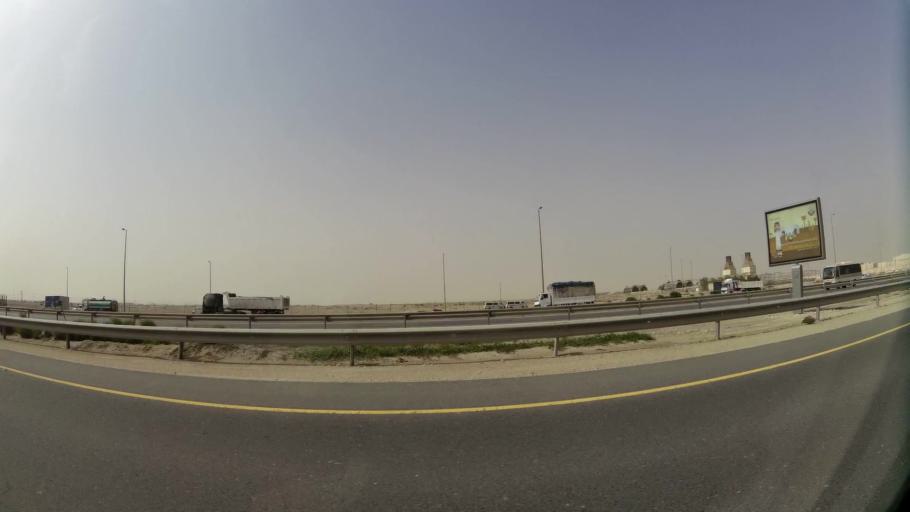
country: QA
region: Baladiyat ar Rayyan
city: Ar Rayyan
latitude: 25.2030
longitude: 51.3929
